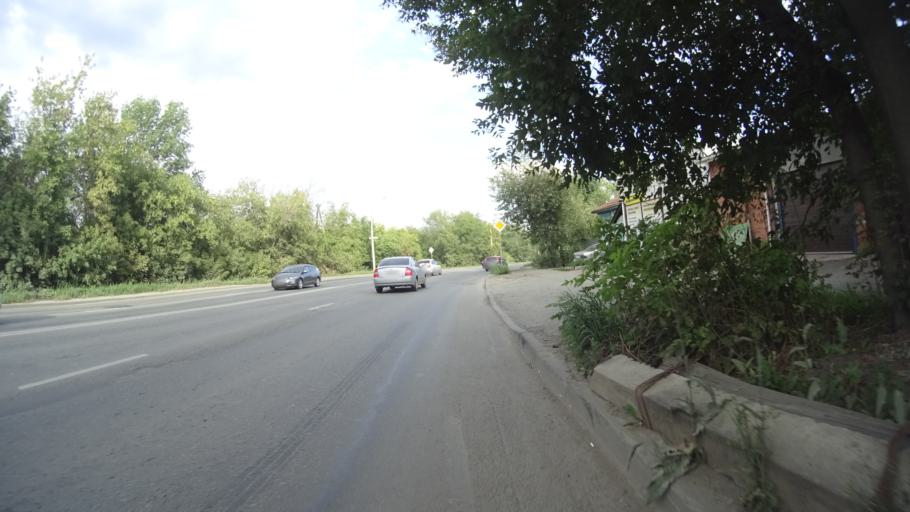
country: RU
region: Chelyabinsk
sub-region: Gorod Chelyabinsk
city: Chelyabinsk
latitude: 55.1984
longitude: 61.3652
